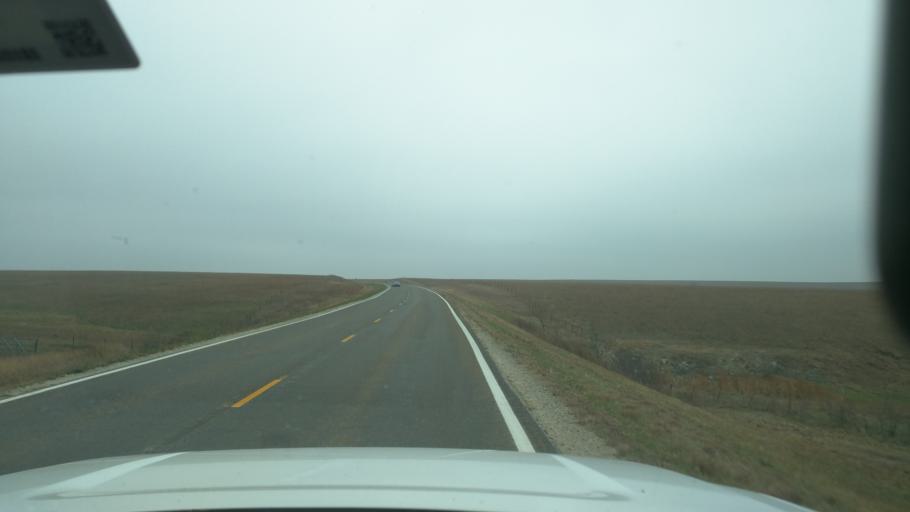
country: US
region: Kansas
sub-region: Morris County
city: Council Grove
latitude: 38.6608
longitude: -96.2752
